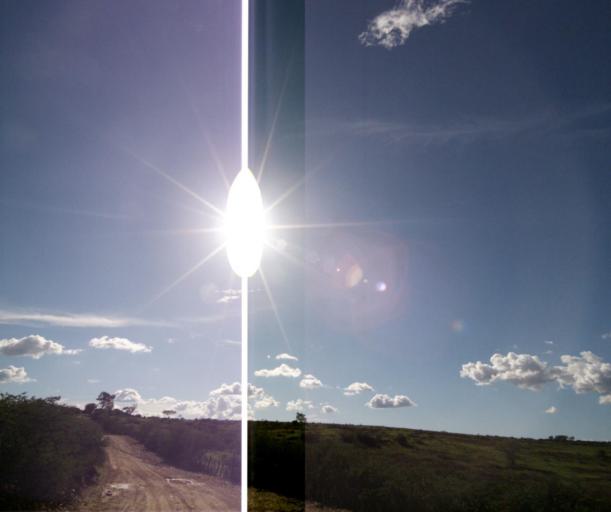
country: BR
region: Bahia
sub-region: Tanhacu
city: Tanhacu
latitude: -14.1846
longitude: -40.9354
